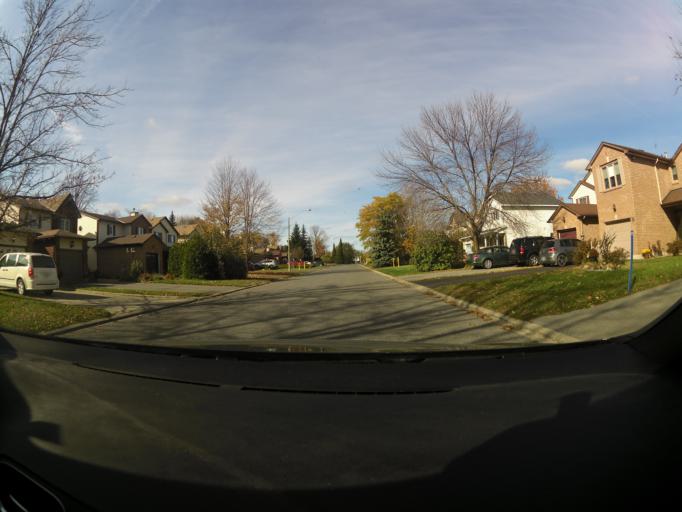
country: CA
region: Ontario
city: Bells Corners
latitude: 45.2752
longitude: -75.9197
